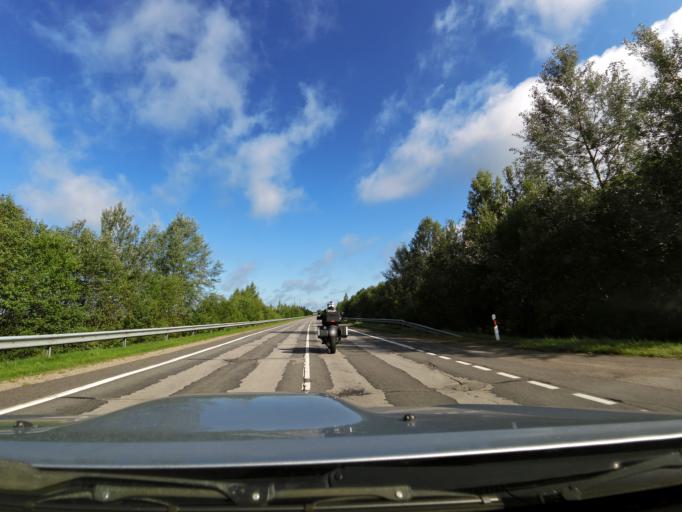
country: LT
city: Nemencine
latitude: 55.0099
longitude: 25.3460
